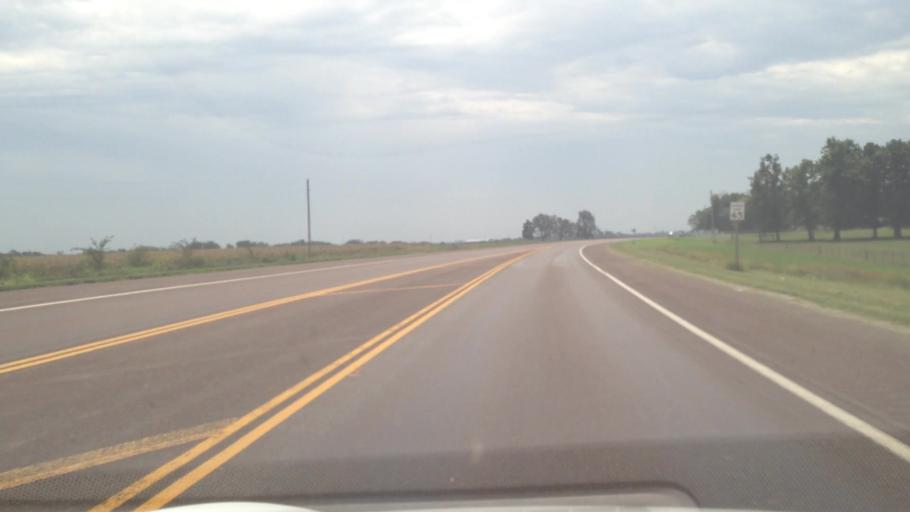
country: US
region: Kansas
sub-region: Crawford County
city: Girard
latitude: 37.4678
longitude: -94.8336
